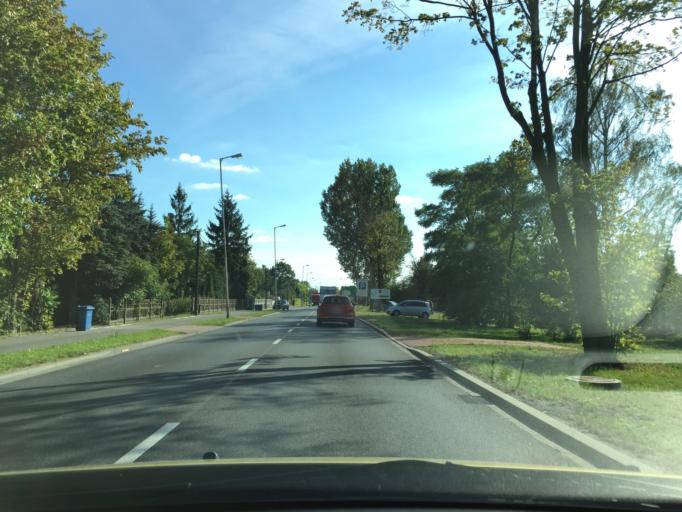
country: PL
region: Greater Poland Voivodeship
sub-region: Kalisz
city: Kalisz
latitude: 51.7861
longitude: 18.0901
